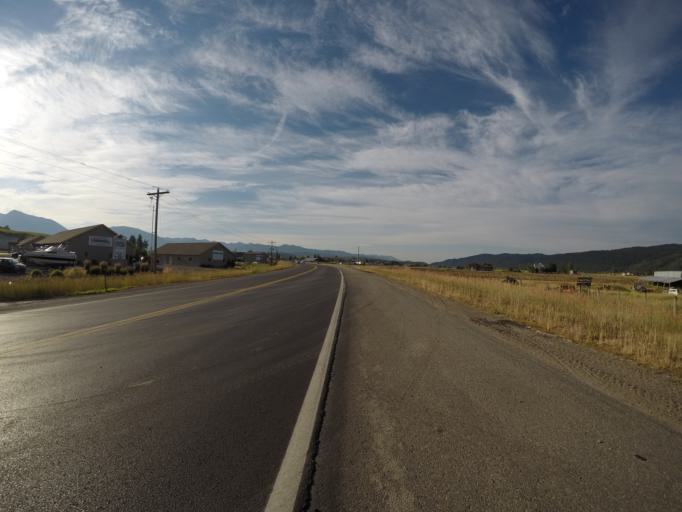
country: US
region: Wyoming
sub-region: Lincoln County
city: Afton
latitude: 42.9278
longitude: -111.0067
